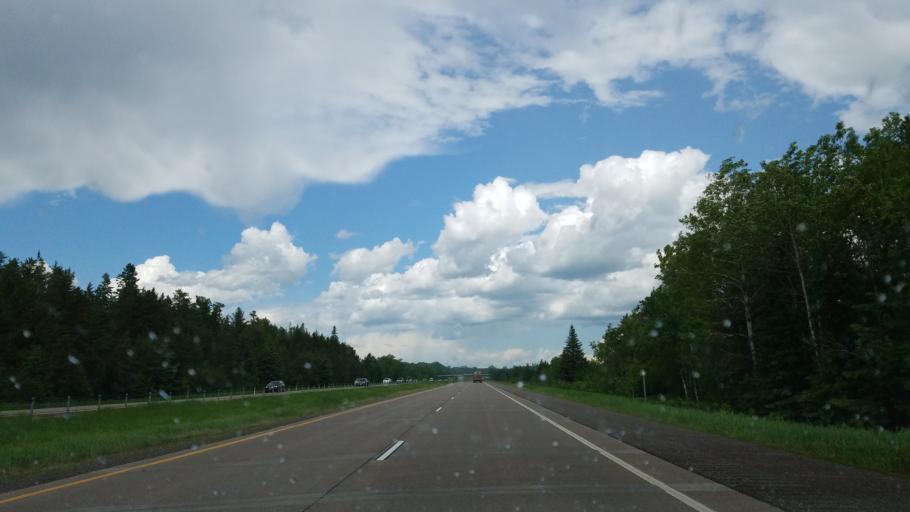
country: US
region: Minnesota
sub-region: Carlton County
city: Moose Lake
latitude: 46.4913
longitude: -92.6974
